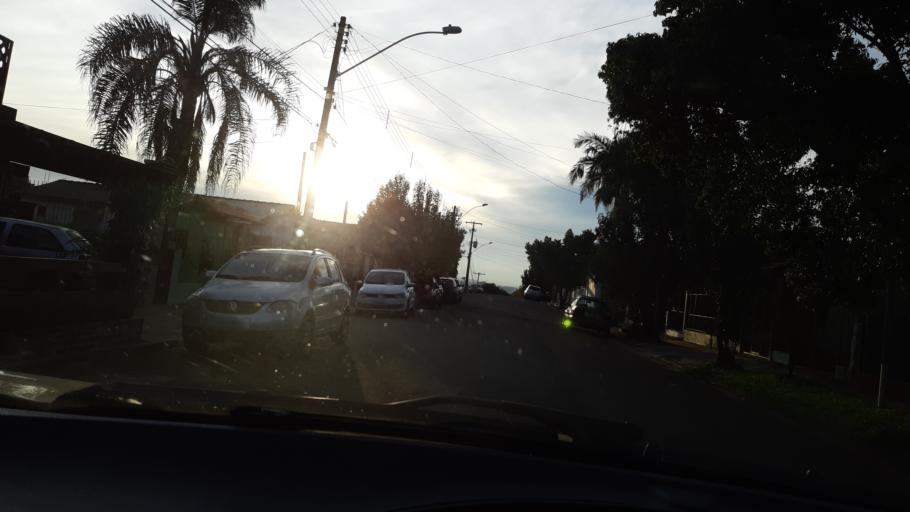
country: BR
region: Rio Grande do Sul
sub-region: Sao Leopoldo
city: Sao Leopoldo
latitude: -29.7881
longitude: -51.1302
